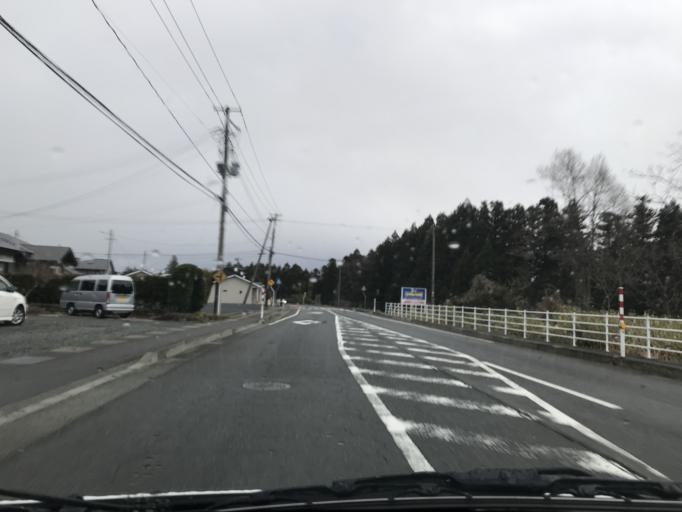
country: JP
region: Iwate
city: Mizusawa
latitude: 39.1960
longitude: 141.1048
